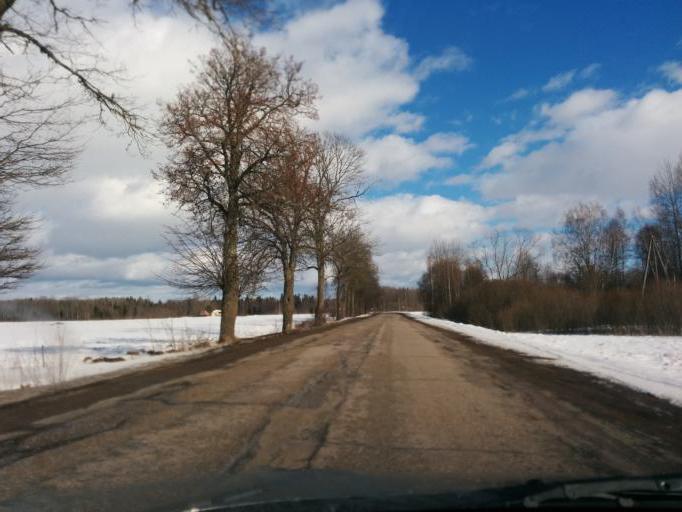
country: LV
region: Gulbenes Rajons
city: Gulbene
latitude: 57.1706
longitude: 26.7984
